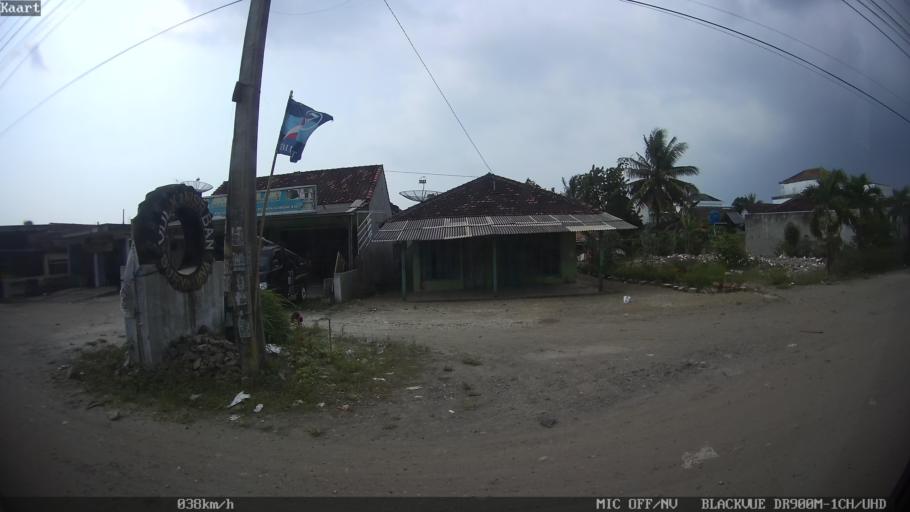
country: ID
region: Lampung
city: Gadingrejo
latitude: -5.3766
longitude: 105.0362
